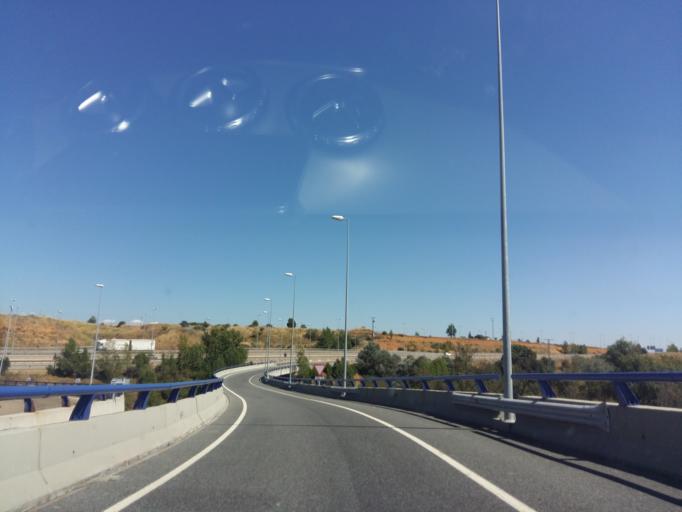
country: ES
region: Castille and Leon
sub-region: Provincia de Leon
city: Valverde de la Virgen
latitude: 42.5670
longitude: -5.6540
